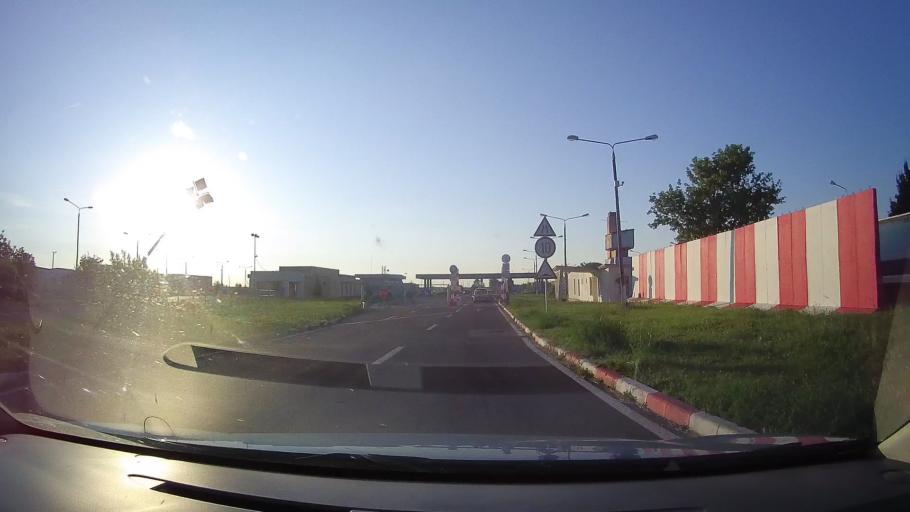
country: RO
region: Timis
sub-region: Comuna Moravita
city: Moravita
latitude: 45.2317
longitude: 21.2731
